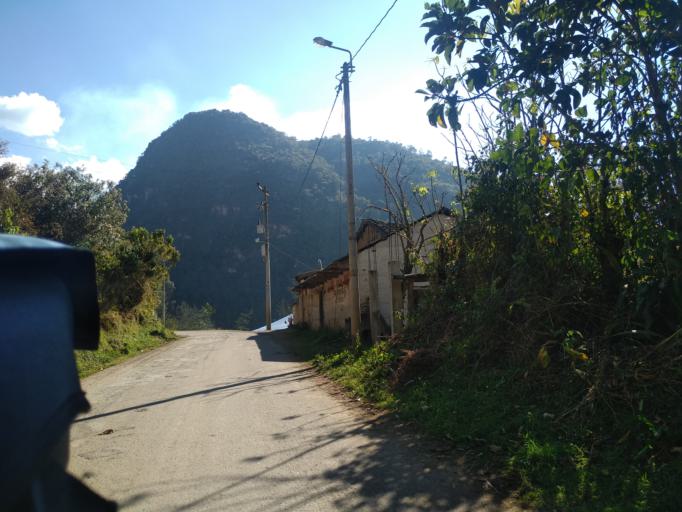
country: PE
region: Amazonas
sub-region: Provincia de Chachapoyas
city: Montevideo
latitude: -6.7190
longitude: -77.8219
